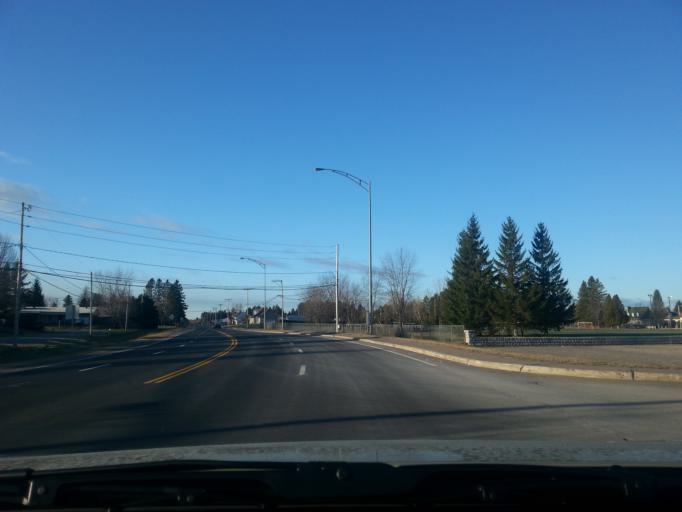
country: CA
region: Quebec
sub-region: Capitale-Nationale
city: Saint-Marc-des-Carrieres
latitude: 46.6871
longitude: -72.0600
